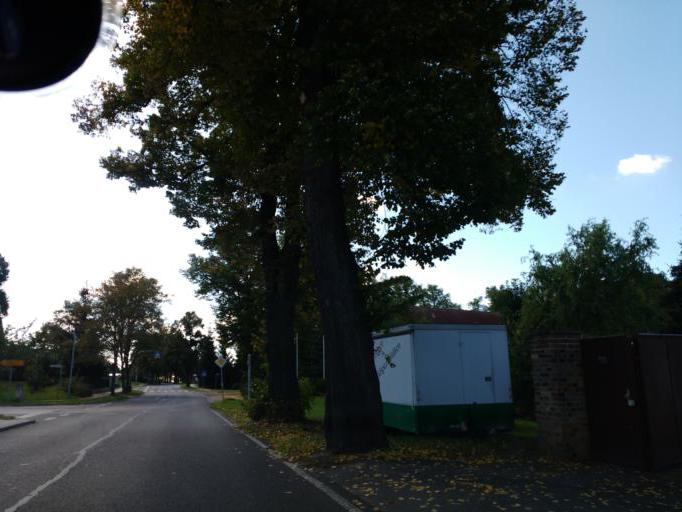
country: DE
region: Brandenburg
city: Mittenwalde
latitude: 52.2457
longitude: 13.5629
